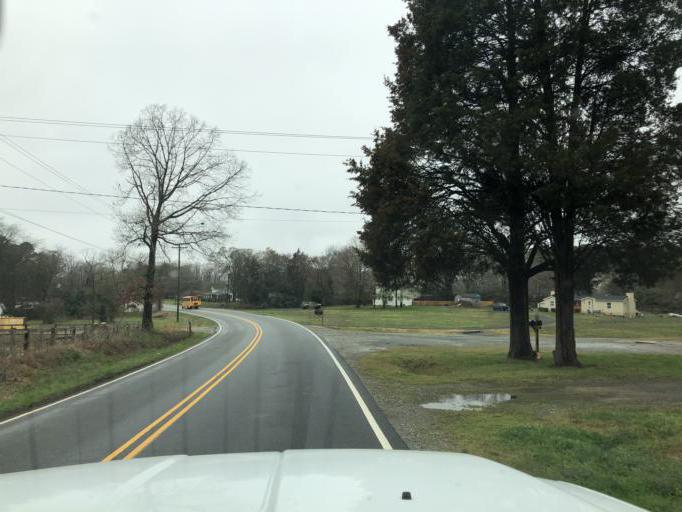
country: US
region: North Carolina
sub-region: Gaston County
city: Mount Holly
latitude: 35.3359
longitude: -80.9211
